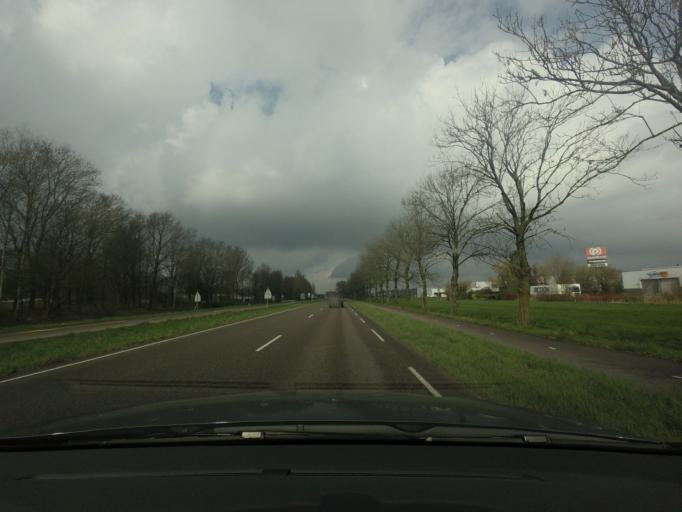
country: NL
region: North Holland
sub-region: Gemeente Aalsmeer
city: Aalsmeer
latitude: 52.2561
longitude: 4.7747
